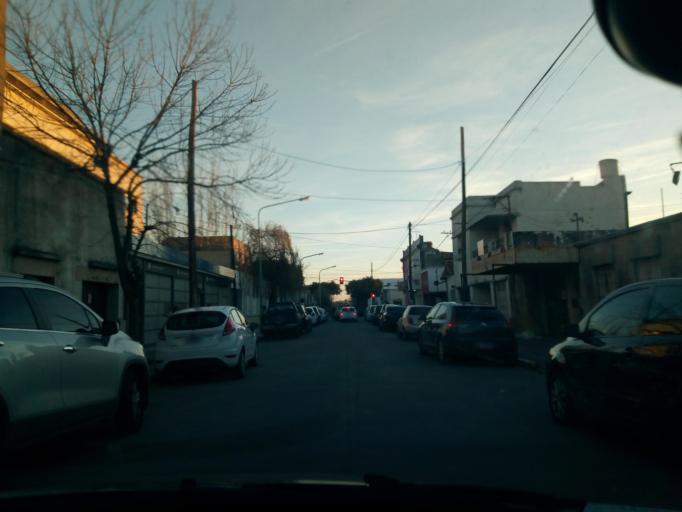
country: AR
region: Buenos Aires
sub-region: Partido de Ensenada
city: Ensenada
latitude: -34.8595
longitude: -57.9047
